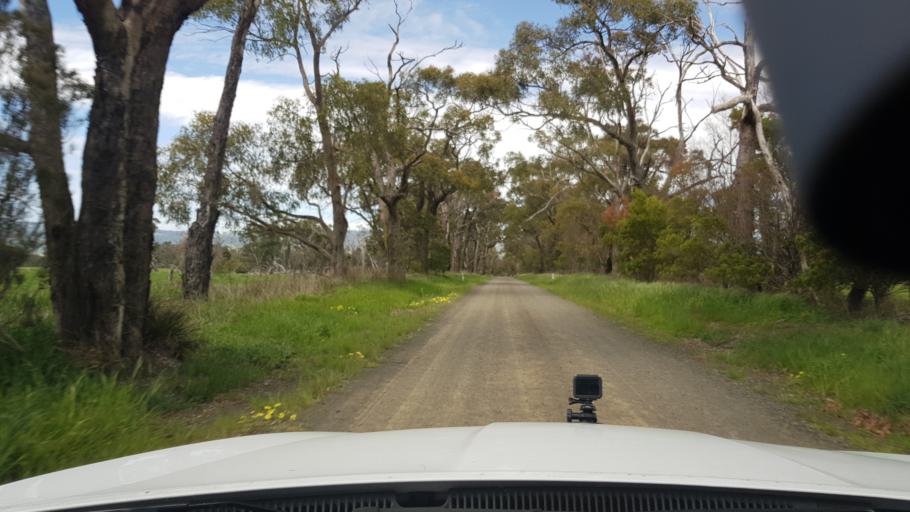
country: AU
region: Victoria
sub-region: Latrobe
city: Moe
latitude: -38.1589
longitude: 146.1358
